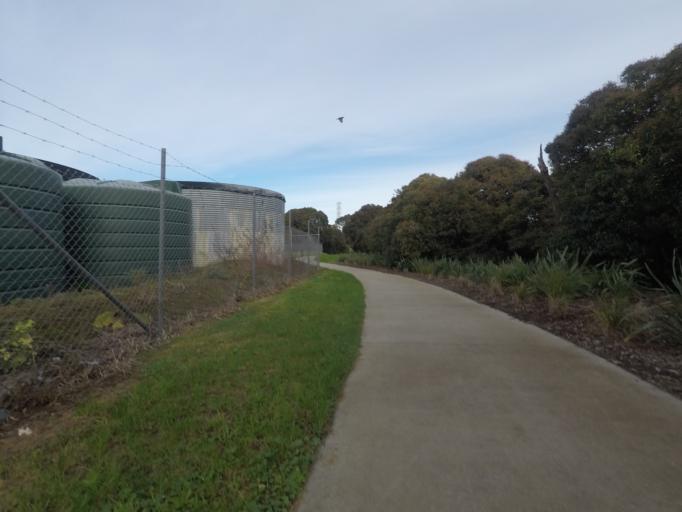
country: NZ
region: Auckland
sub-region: Auckland
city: Mangere
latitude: -36.9476
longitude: 174.8048
